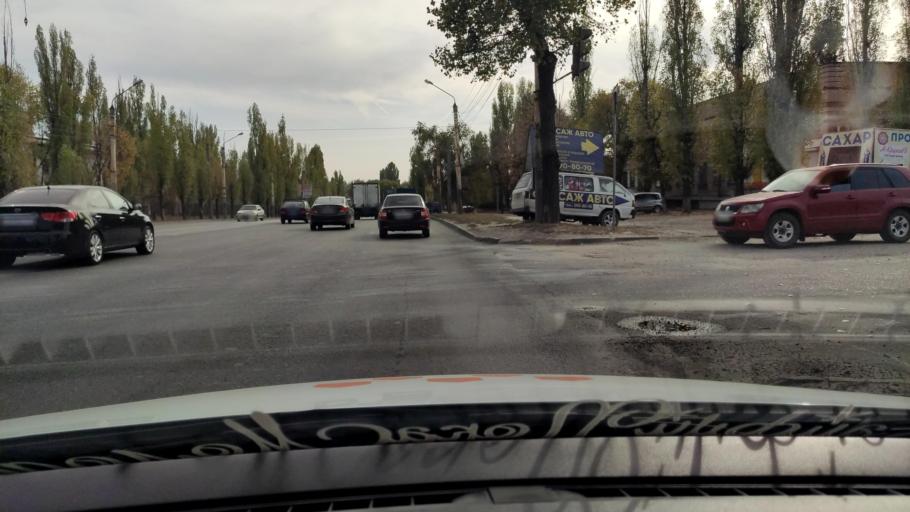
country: RU
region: Voronezj
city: Voronezh
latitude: 51.6265
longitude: 39.2312
